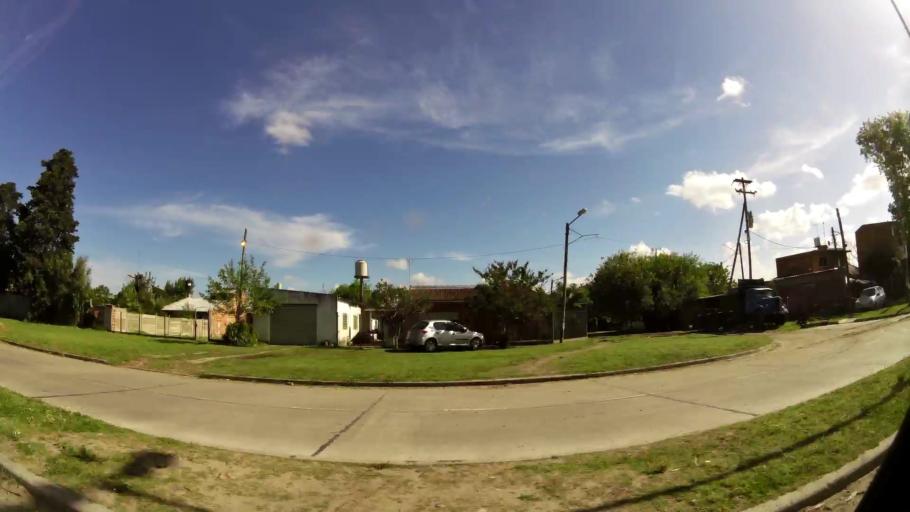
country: AR
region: Buenos Aires
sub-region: Partido de Quilmes
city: Quilmes
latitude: -34.8077
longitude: -58.2193
